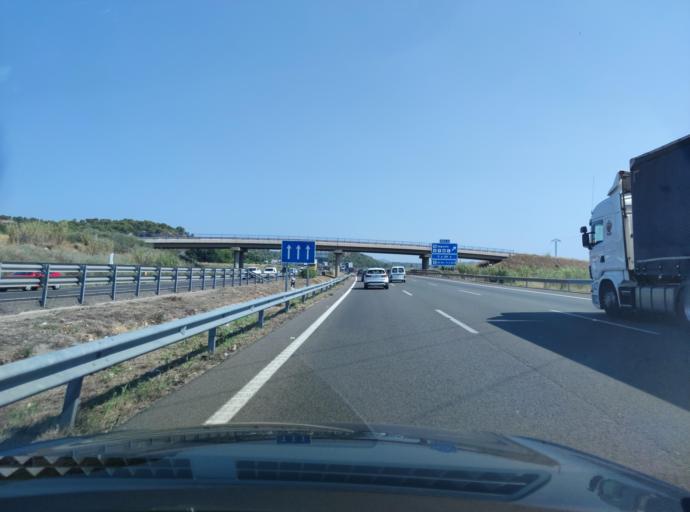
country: ES
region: Valencia
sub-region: Provincia de Valencia
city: Pucol
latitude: 39.6416
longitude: -0.3005
